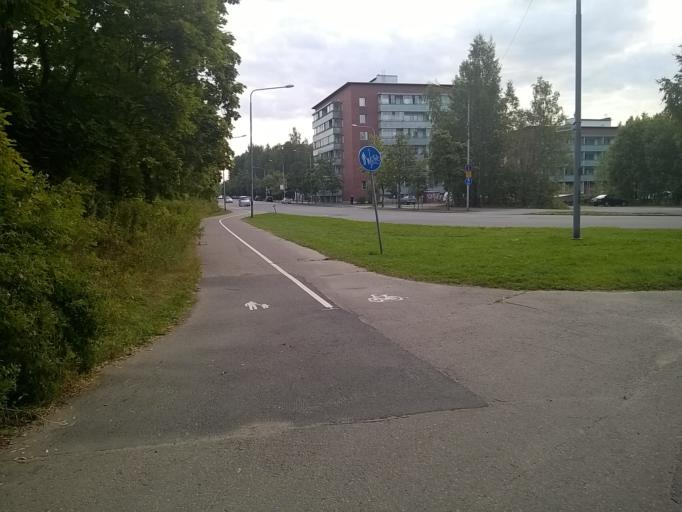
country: FI
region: Pirkanmaa
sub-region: Tampere
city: Tampere
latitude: 61.4485
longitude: 23.8383
